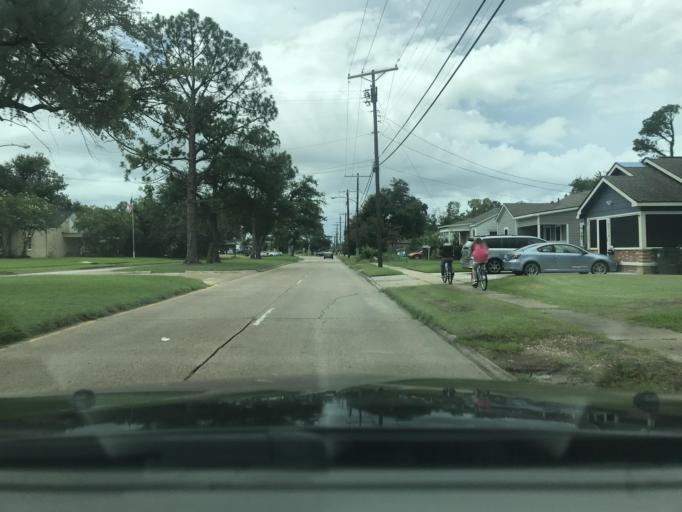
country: US
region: Louisiana
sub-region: Calcasieu Parish
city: Lake Charles
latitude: 30.2050
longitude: -93.2044
